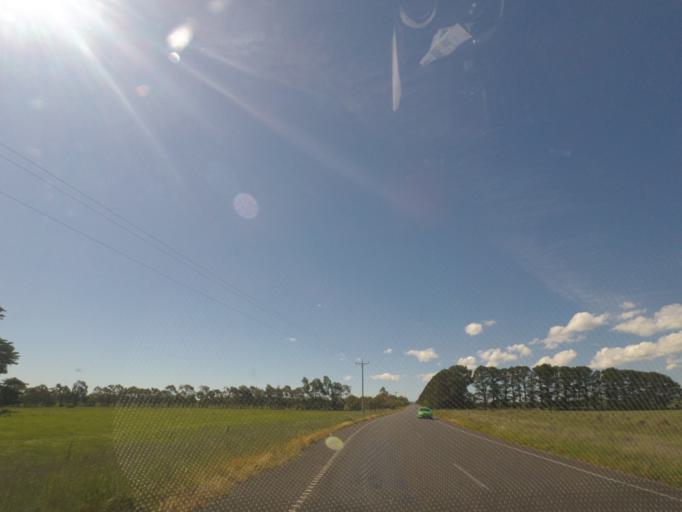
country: AU
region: Victoria
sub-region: Moorabool
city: Bacchus Marsh
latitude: -37.7347
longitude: 144.2178
